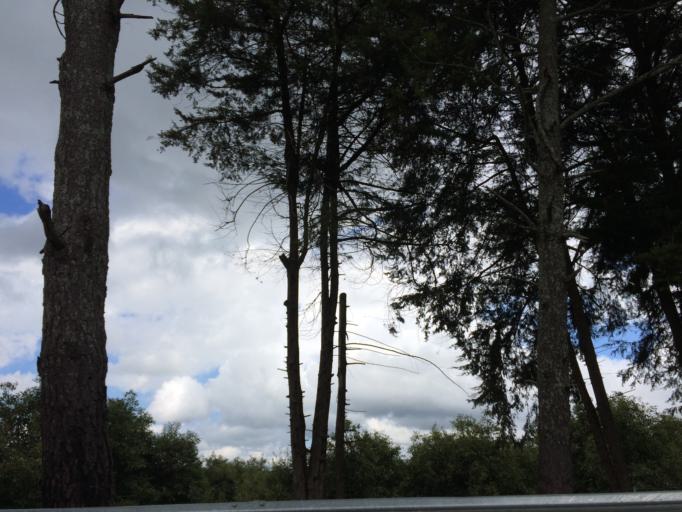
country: MX
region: Michoacan
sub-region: Uruapan
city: Santa Ana Zirosto
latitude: 19.5507
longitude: -102.3147
